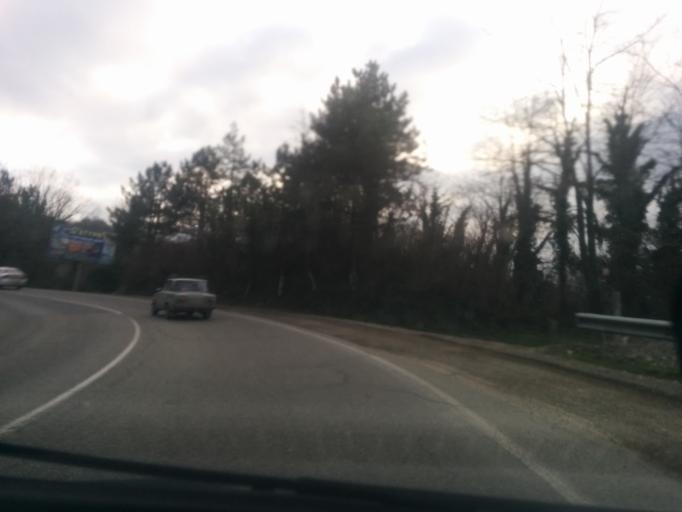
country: RU
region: Krasnodarskiy
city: Agoy
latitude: 44.1402
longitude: 39.0543
